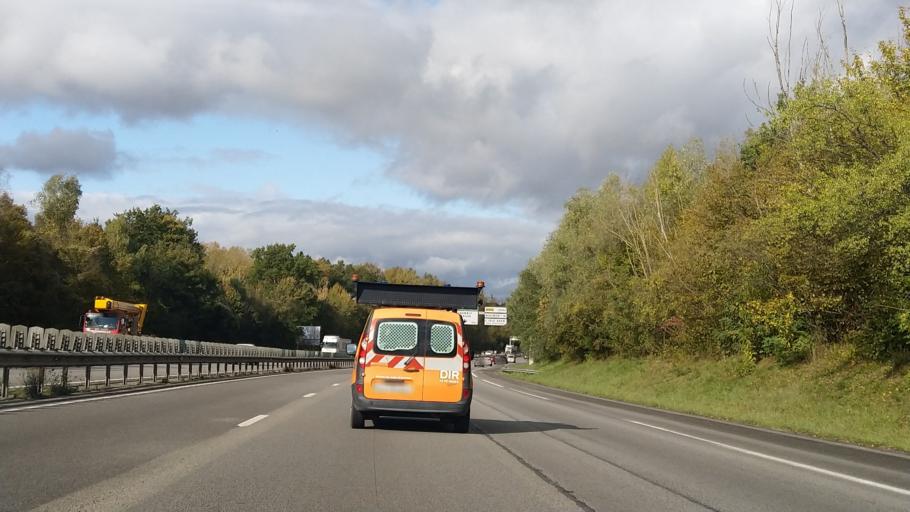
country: FR
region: Ile-de-France
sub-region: Departement du Val-d'Oise
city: Mours
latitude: 49.1159
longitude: 2.2541
